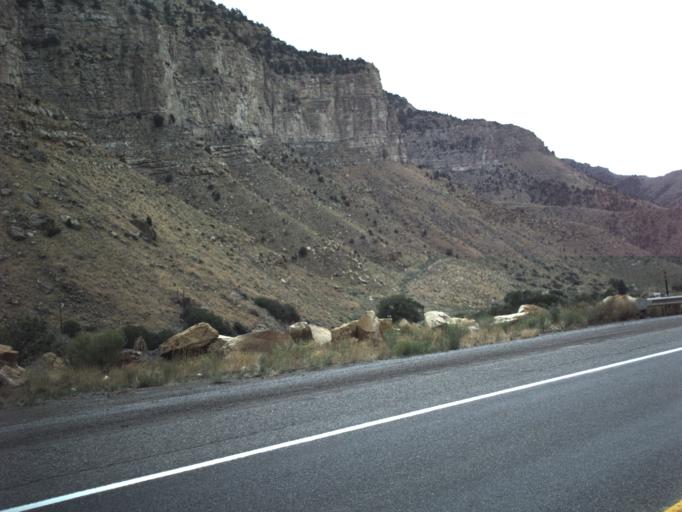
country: US
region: Utah
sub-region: Carbon County
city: Helper
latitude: 39.7450
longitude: -110.8813
